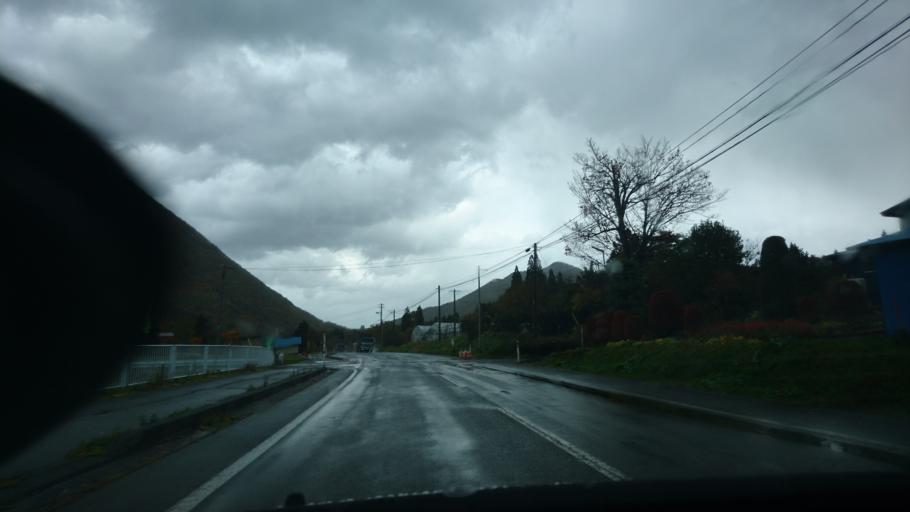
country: JP
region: Iwate
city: Shizukuishi
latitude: 39.6021
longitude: 140.9286
